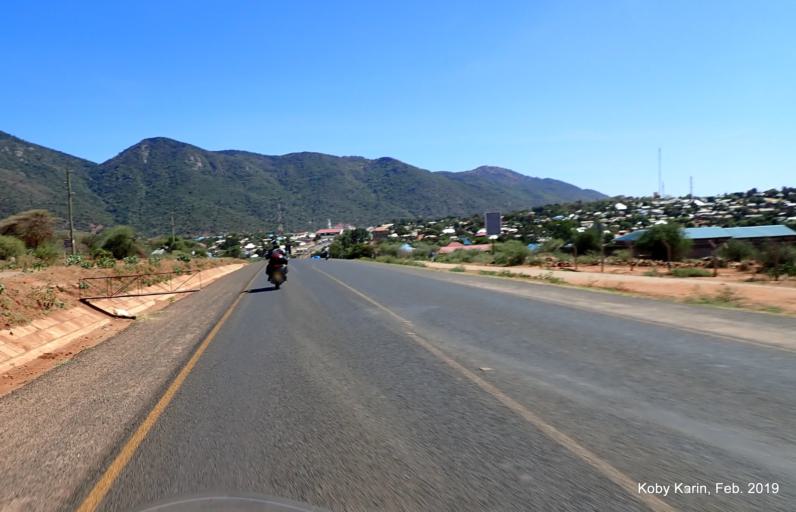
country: TZ
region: Arusha
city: Namanga
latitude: -2.5599
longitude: 36.7803
